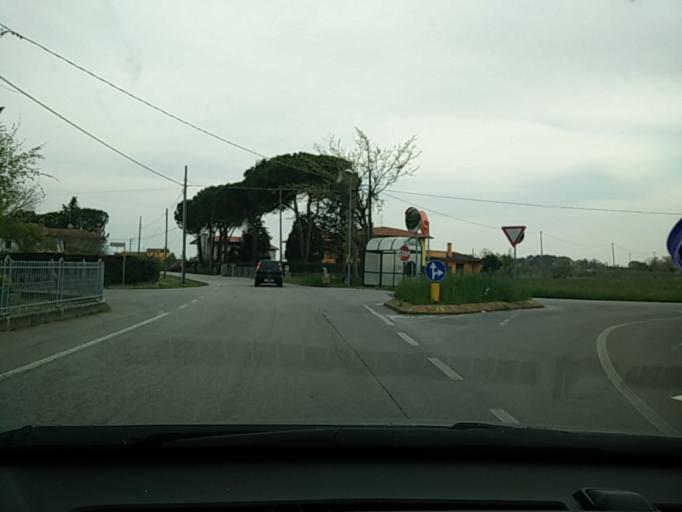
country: IT
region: Veneto
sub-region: Provincia di Treviso
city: Talponada
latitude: 45.6973
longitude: 12.5098
